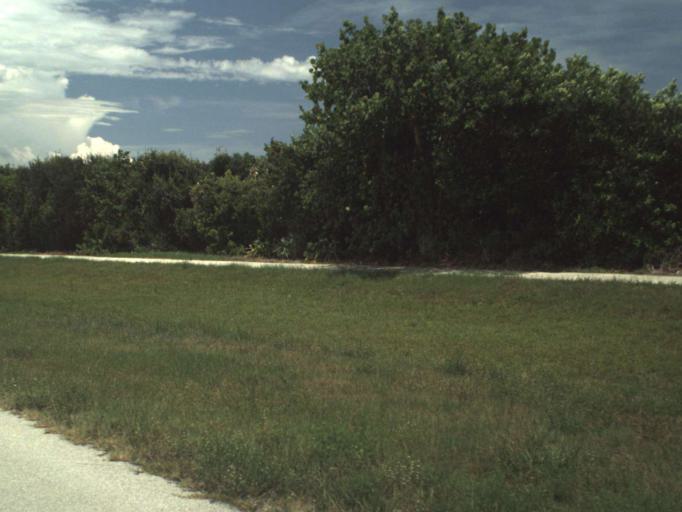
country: US
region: Florida
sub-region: Saint Lucie County
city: Hutchinson Island South
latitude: 27.2952
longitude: -80.2163
